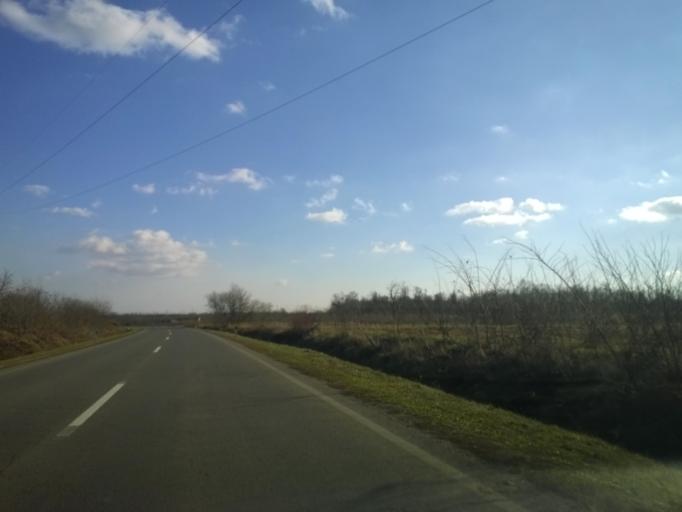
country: RS
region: Central Serbia
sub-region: Podunavski Okrug
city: Smederevo
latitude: 44.6126
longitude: 20.9080
